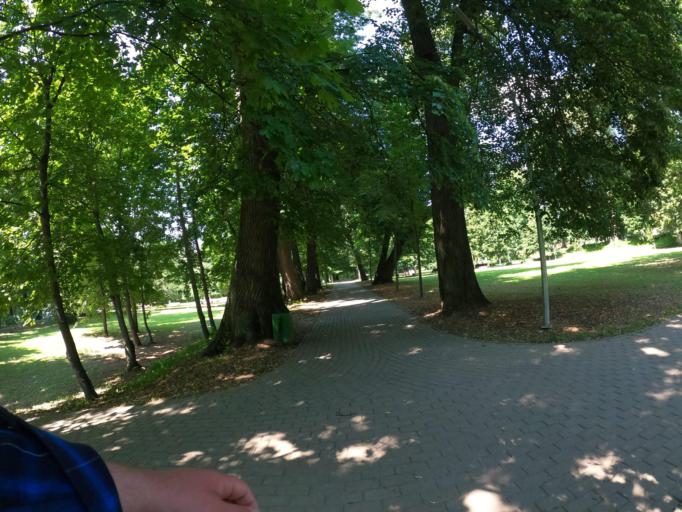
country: RU
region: Kaluga
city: Obninsk
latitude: 55.1244
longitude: 36.5933
